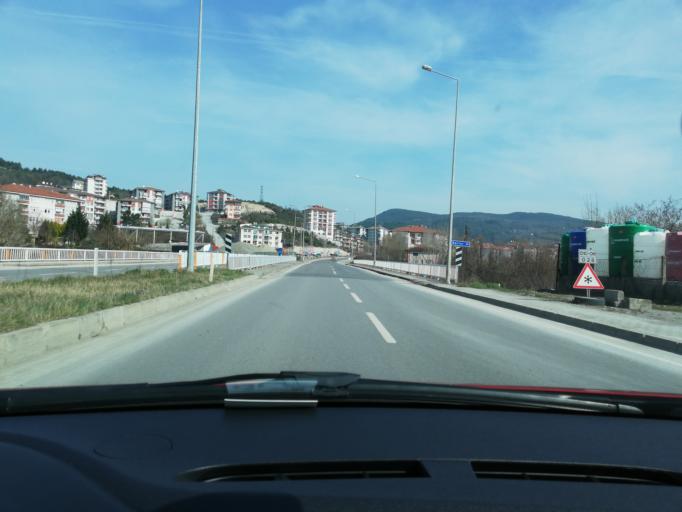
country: TR
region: Bartin
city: Bartin
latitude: 41.6406
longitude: 32.3550
